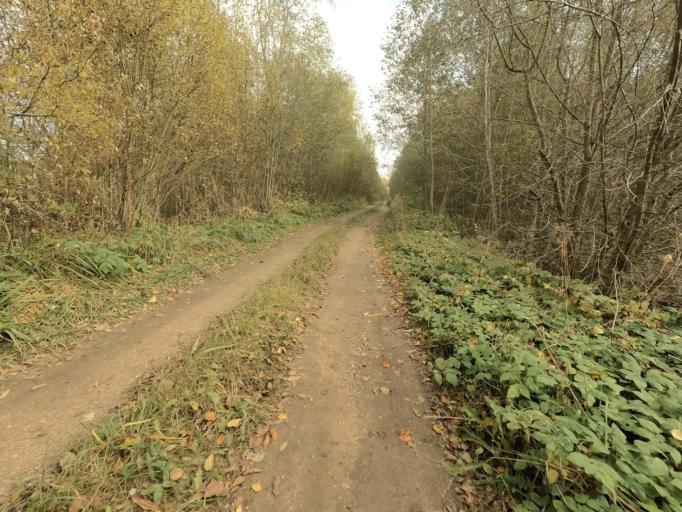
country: RU
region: Novgorod
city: Pankovka
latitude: 58.8799
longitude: 30.8144
